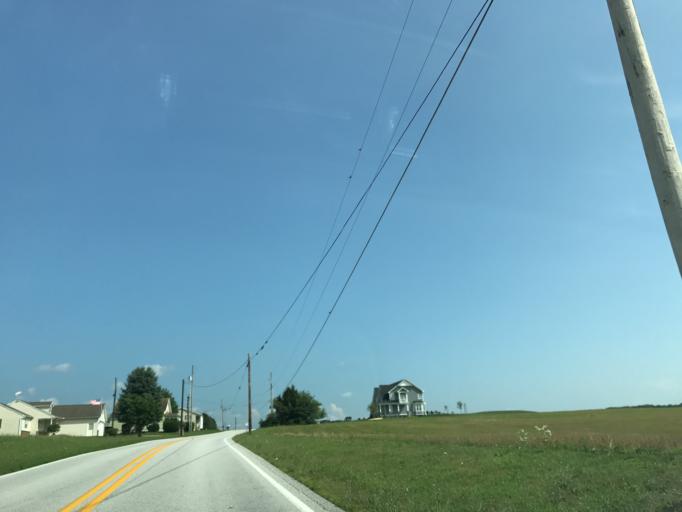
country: US
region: Pennsylvania
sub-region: York County
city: Pennville
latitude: 39.7441
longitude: -77.0190
